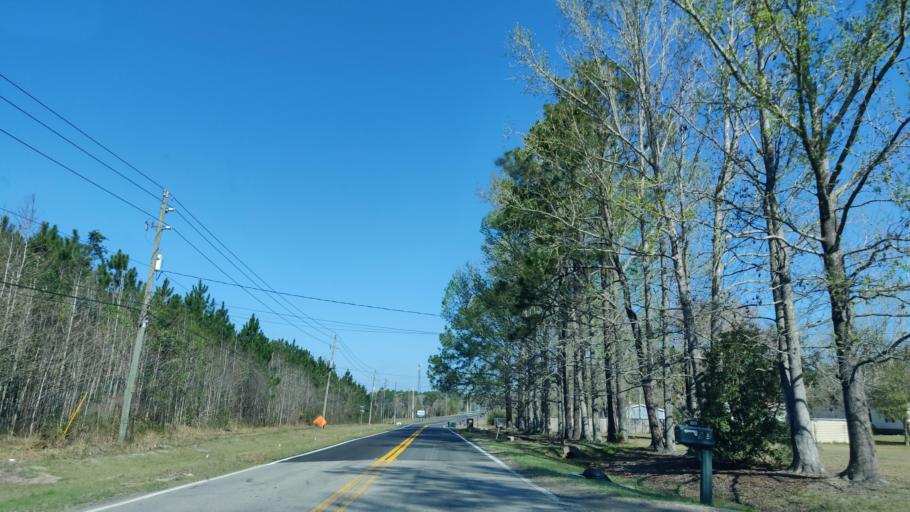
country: US
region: Florida
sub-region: Duval County
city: Baldwin
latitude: 30.2861
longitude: -81.9653
